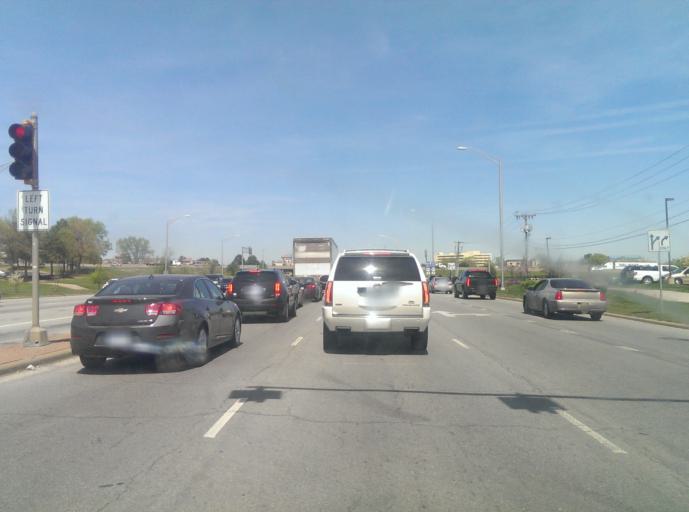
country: US
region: Kansas
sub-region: Johnson County
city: Overland Park
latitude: 38.9293
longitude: -94.6677
